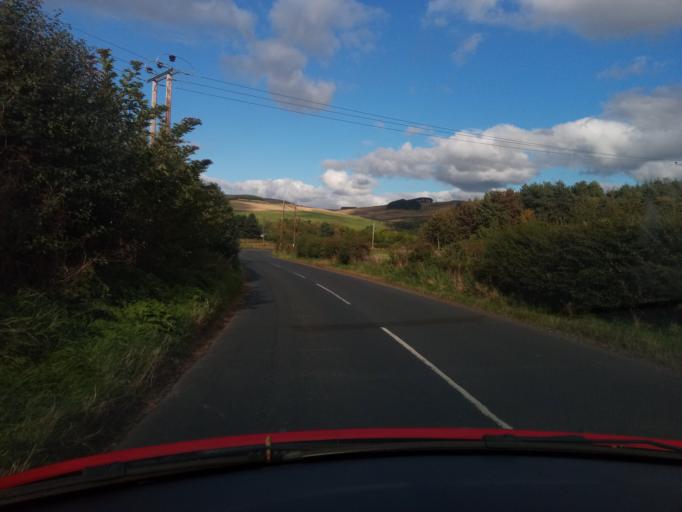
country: GB
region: Scotland
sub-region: The Scottish Borders
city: Kelso
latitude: 55.5199
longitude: -2.3547
